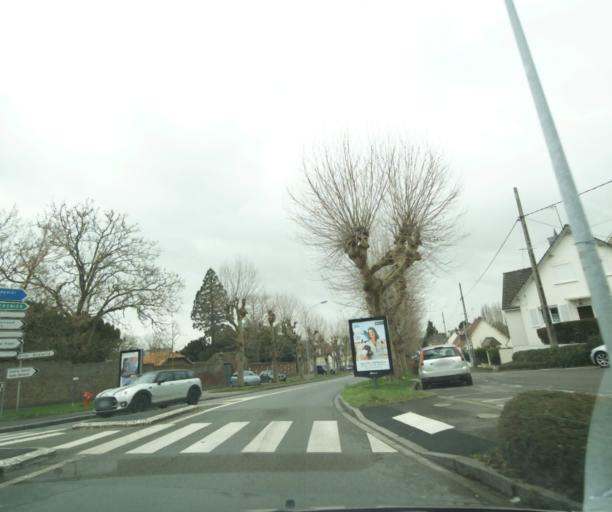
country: FR
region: Picardie
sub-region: Departement de l'Oise
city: Noyon
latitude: 49.5836
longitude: 2.9964
